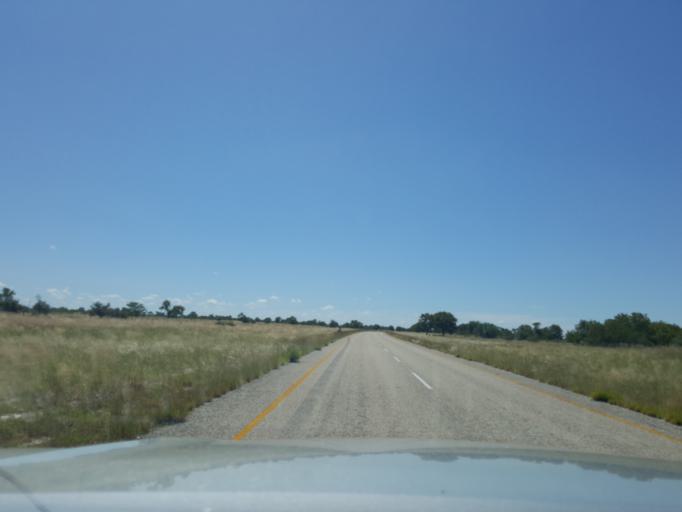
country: BW
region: Central
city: Gweta
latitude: -20.2130
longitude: 25.0883
